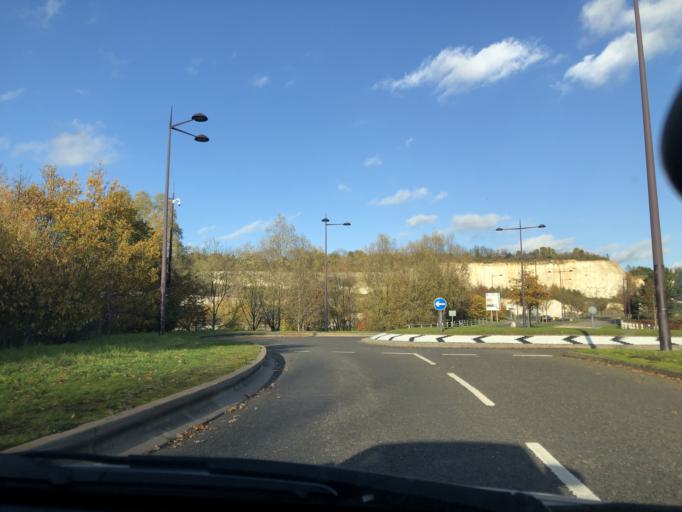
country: GB
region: England
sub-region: Kent
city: Stone
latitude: 51.4410
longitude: 0.2650
